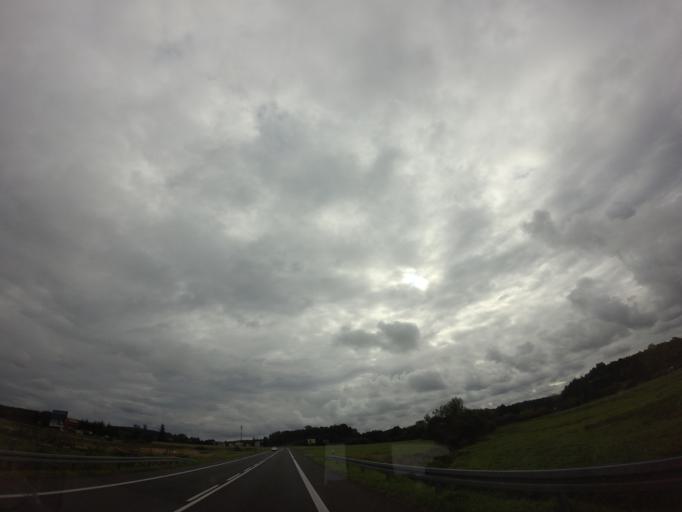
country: PL
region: West Pomeranian Voivodeship
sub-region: Powiat goleniowski
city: Przybiernow
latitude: 53.7544
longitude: 14.7750
